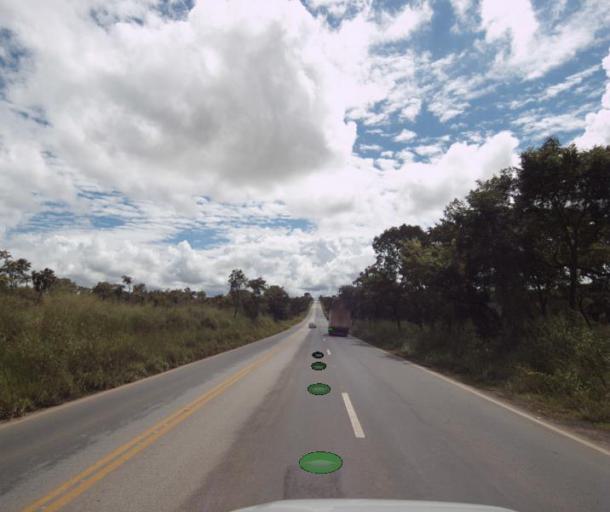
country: BR
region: Goias
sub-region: Uruacu
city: Uruacu
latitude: -14.3508
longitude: -49.1583
